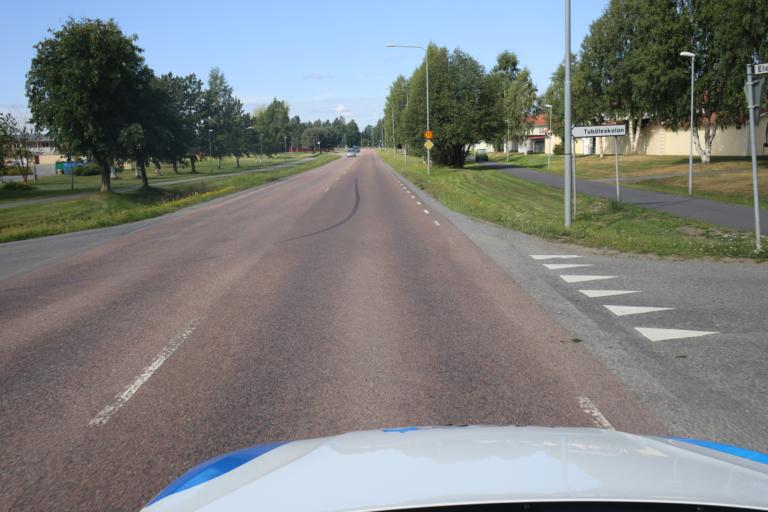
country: SE
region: Vaesterbotten
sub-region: Skelleftea Kommun
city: Skelleftea
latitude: 64.7449
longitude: 20.9830
